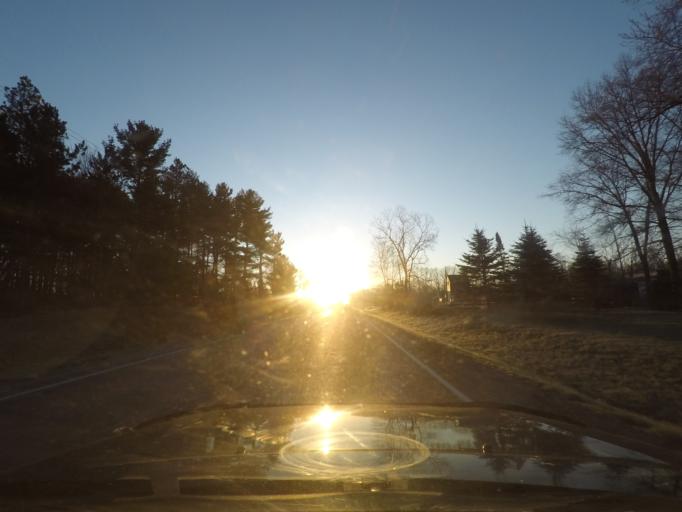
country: US
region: Indiana
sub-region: Marshall County
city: Plymouth
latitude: 41.4490
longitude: -86.3366
